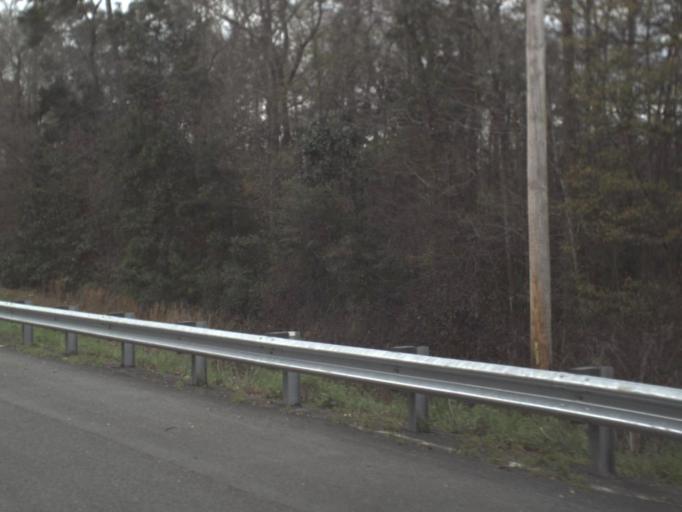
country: US
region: Florida
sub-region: Gadsden County
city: Quincy
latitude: 30.4793
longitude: -84.6261
